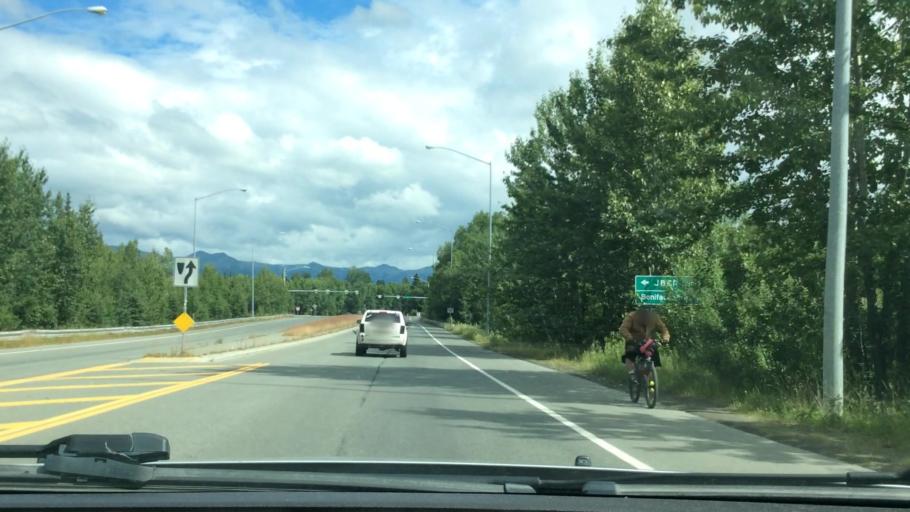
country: US
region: Alaska
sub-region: Anchorage Municipality
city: Anchorage
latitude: 61.2261
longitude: -149.7834
